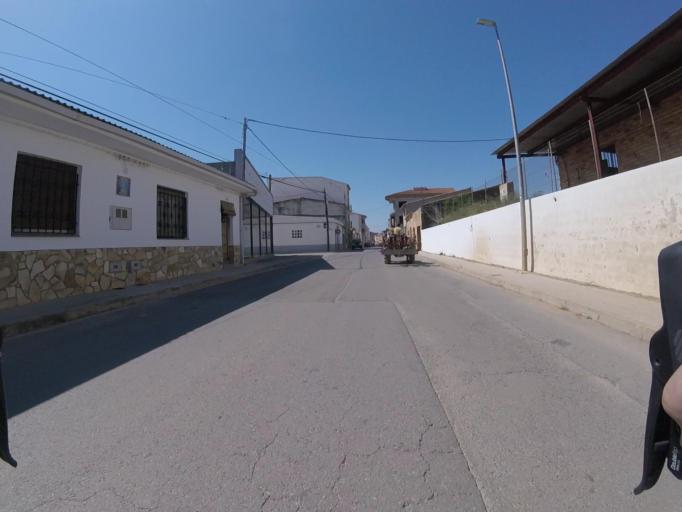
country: ES
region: Valencia
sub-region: Provincia de Castello
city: Benlloch
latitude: 40.2132
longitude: 0.0300
